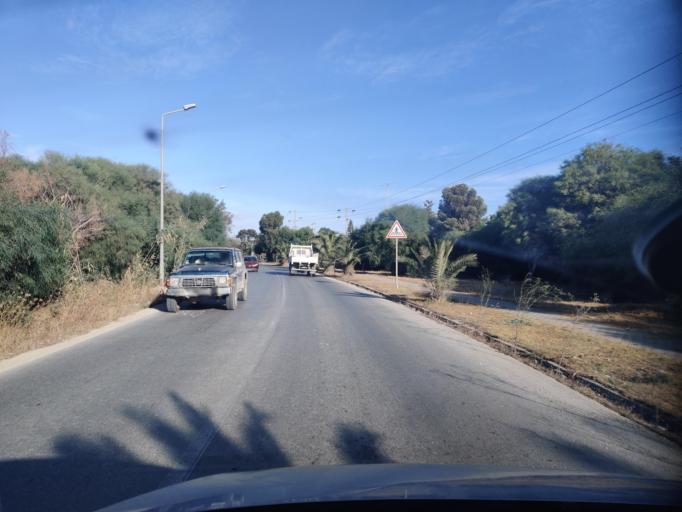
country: TN
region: Tunis
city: Al Marsa
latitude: 36.9390
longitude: 10.2520
